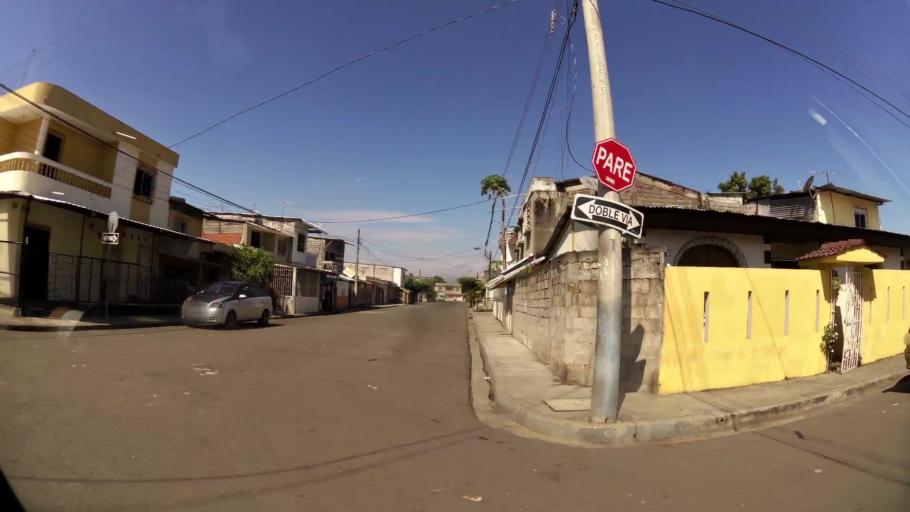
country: EC
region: Guayas
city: Guayaquil
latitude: -2.2143
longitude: -79.9438
